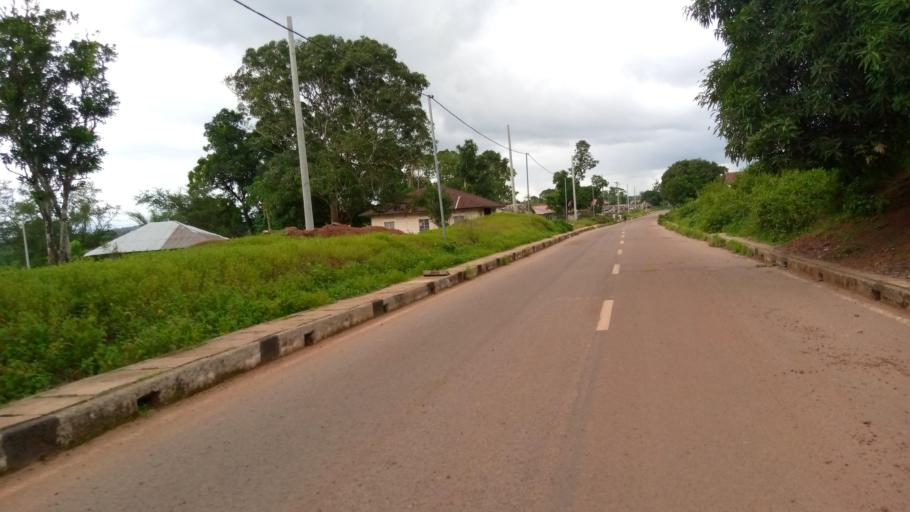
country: SL
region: Southern Province
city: Moyamba
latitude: 8.1635
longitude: -12.4419
